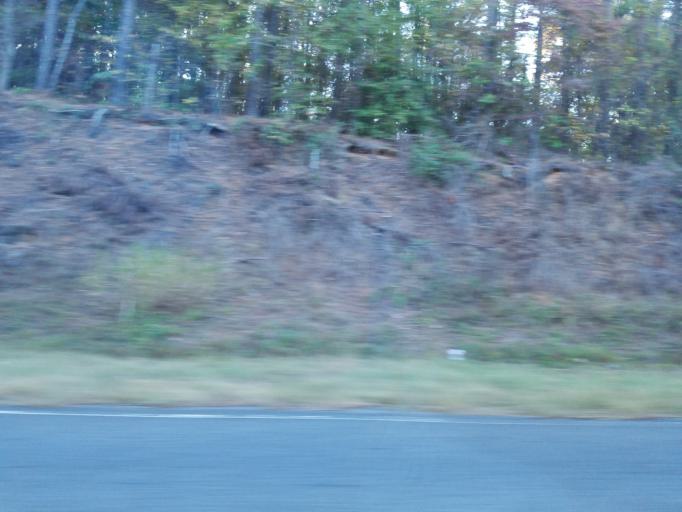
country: US
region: Georgia
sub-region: Bartow County
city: Adairsville
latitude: 34.3185
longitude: -84.9367
